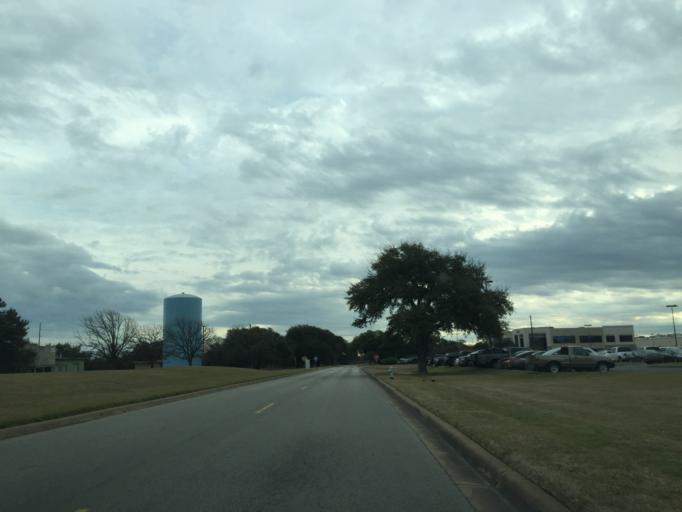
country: US
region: Texas
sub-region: Williamson County
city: Jollyville
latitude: 30.4368
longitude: -97.7543
